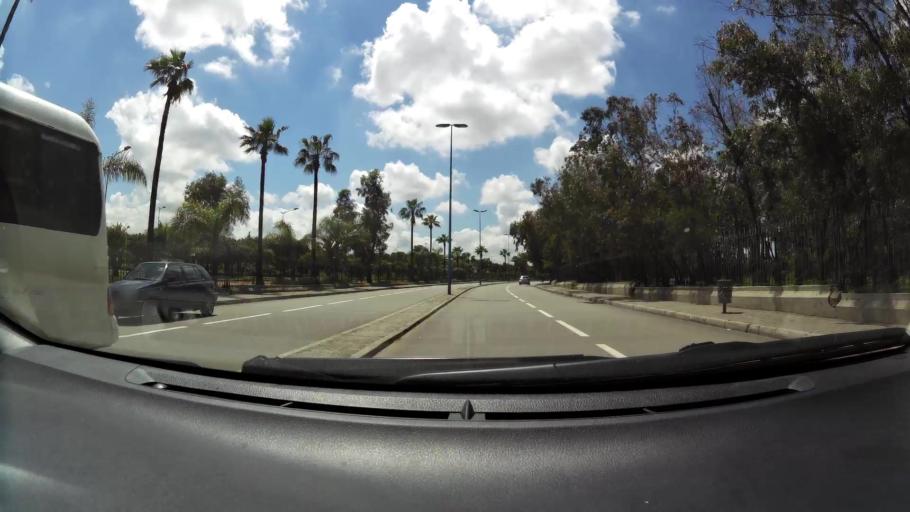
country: MA
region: Grand Casablanca
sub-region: Casablanca
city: Casablanca
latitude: 33.5556
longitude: -7.5666
